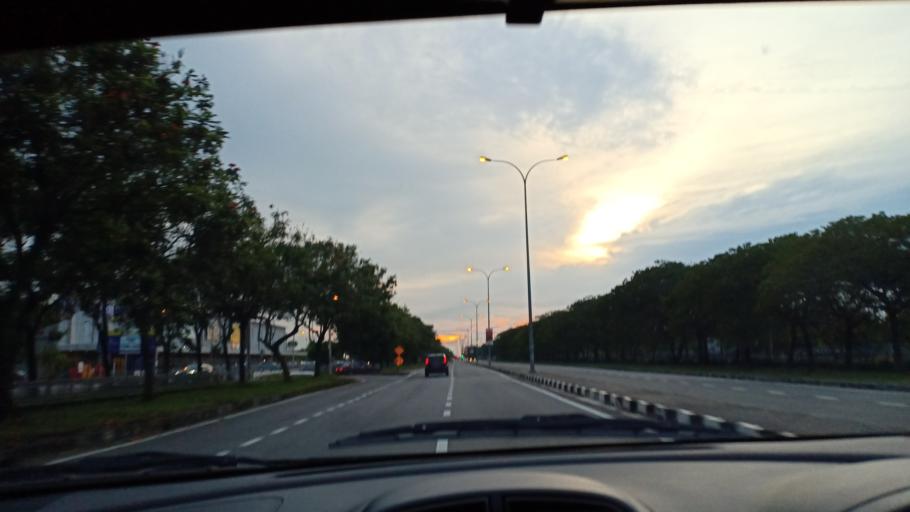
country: MY
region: Penang
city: Tasek Glugor
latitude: 5.5200
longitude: 100.4797
